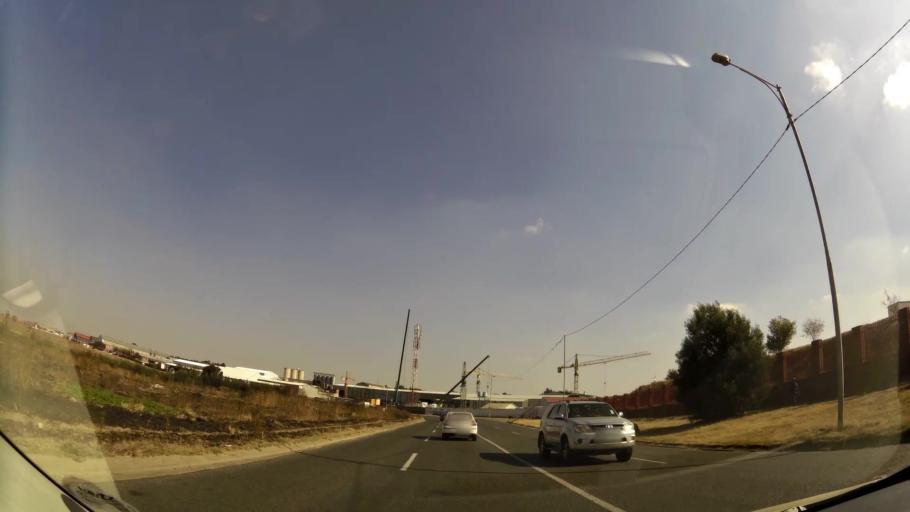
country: ZA
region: Gauteng
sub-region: City of Johannesburg Metropolitan Municipality
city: Roodepoort
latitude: -26.1565
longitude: 27.8061
